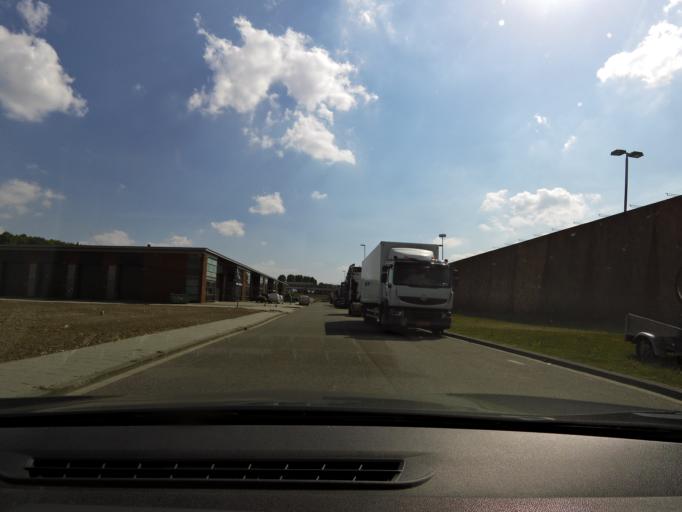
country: NL
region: South Holland
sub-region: Gemeente Albrandswaard
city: Rhoon
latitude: 51.8647
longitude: 4.3816
